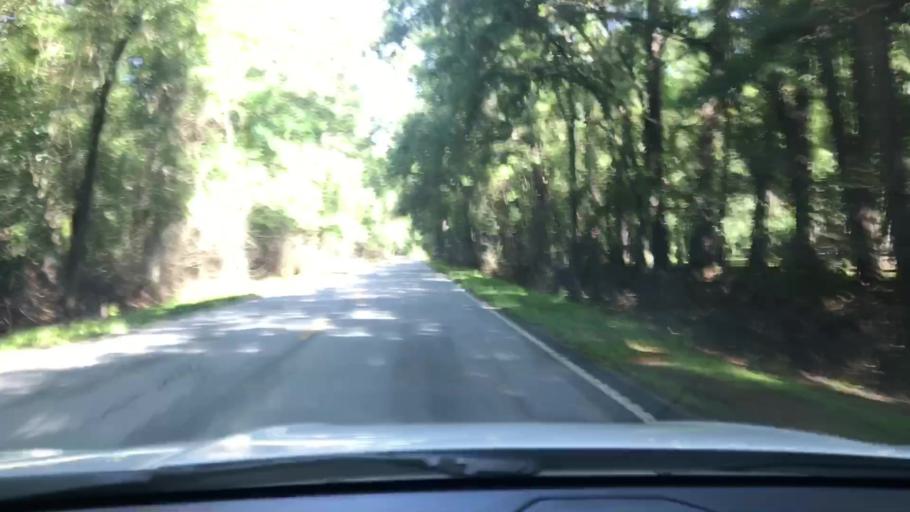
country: US
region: South Carolina
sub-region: Berkeley County
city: Ladson
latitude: 32.9011
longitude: -80.1427
